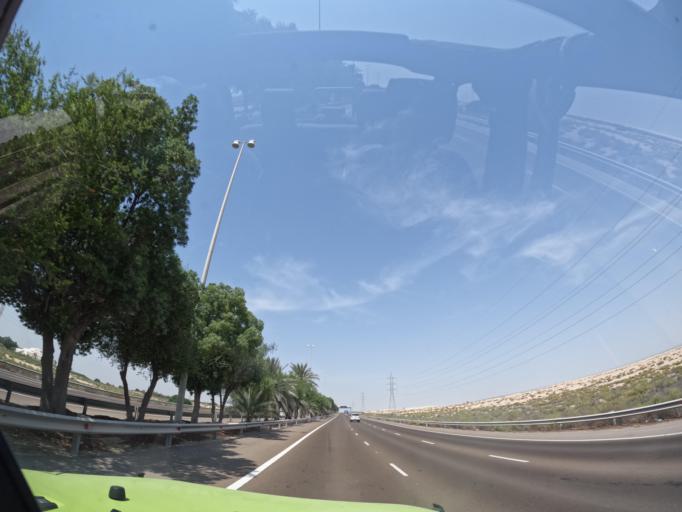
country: AE
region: Abu Dhabi
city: Abu Dhabi
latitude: 24.2344
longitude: 54.7570
